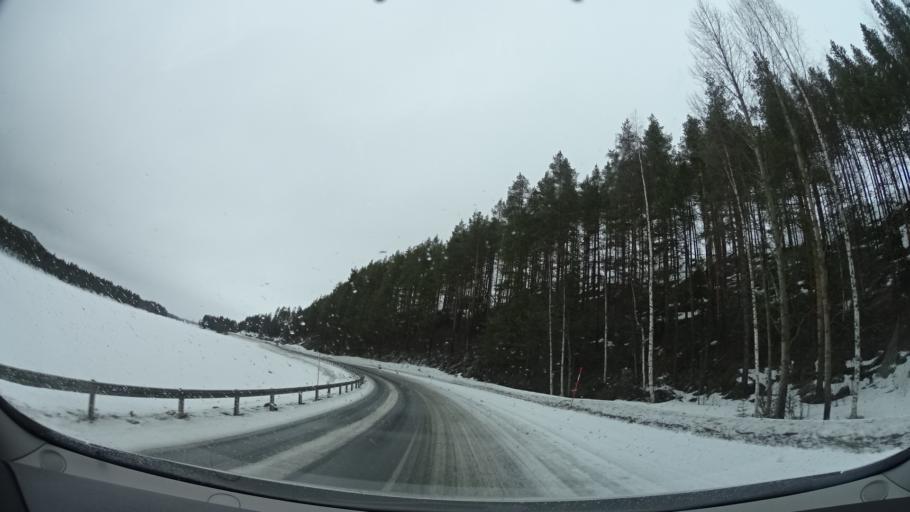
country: SE
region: Vaesterbotten
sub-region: Mala Kommun
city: Mala
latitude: 65.1642
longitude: 18.7807
